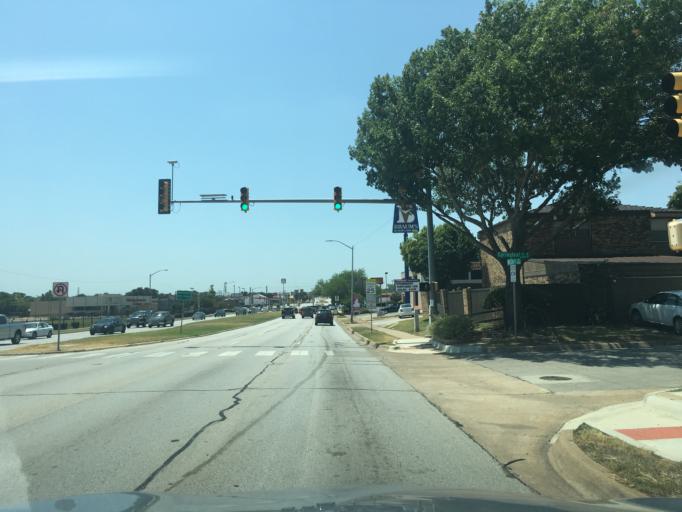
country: US
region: Texas
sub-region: Tarrant County
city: Edgecliff Village
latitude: 32.6570
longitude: -97.3603
